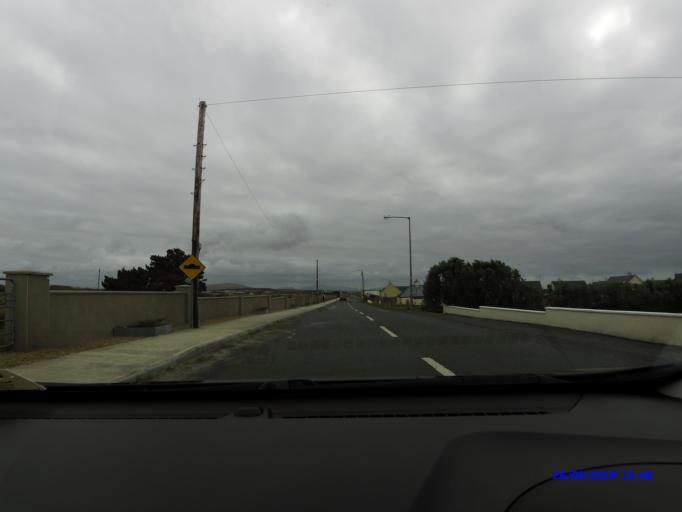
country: IE
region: Connaught
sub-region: Maigh Eo
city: Belmullet
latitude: 54.2176
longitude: -9.9820
